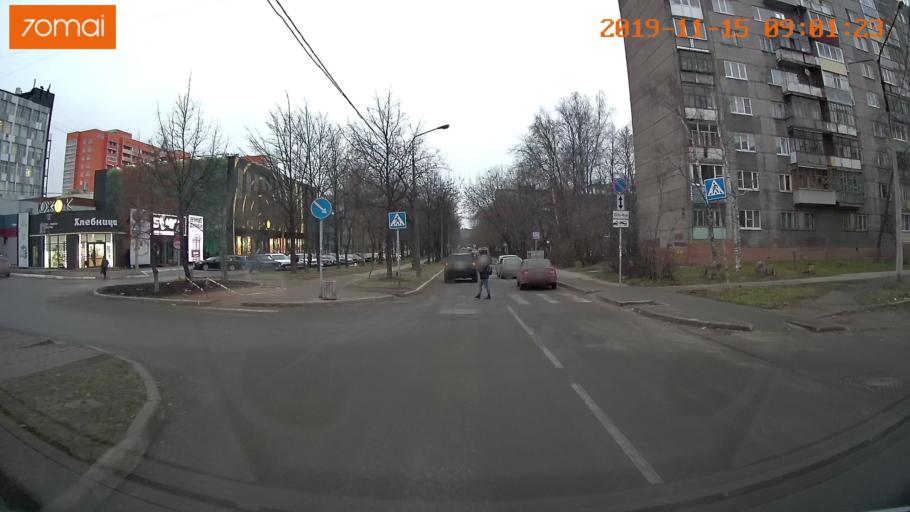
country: RU
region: Vologda
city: Cherepovets
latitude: 59.1321
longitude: 37.9258
